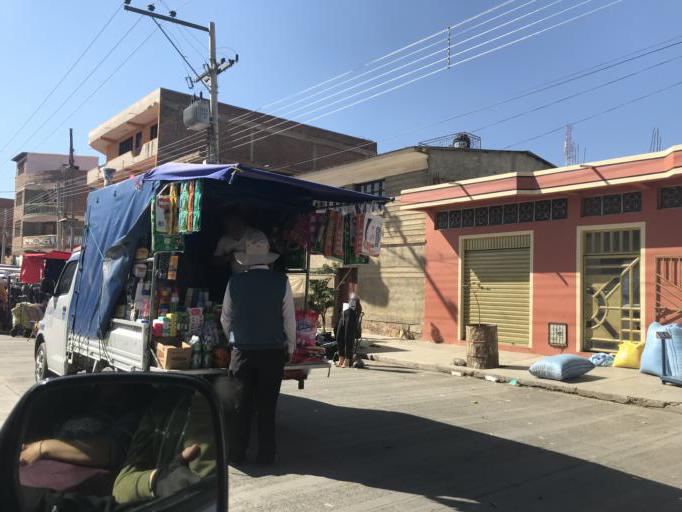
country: BO
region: Cochabamba
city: Punata
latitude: -17.5479
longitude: -65.8408
